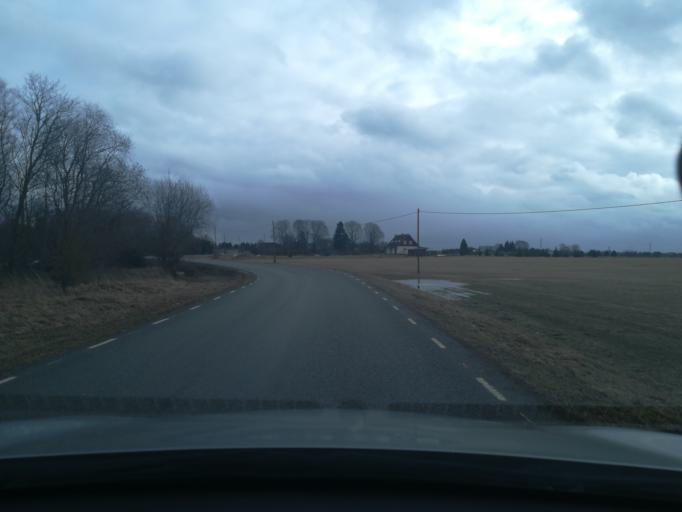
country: EE
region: Harju
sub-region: Saue linn
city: Saue
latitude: 59.3456
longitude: 24.5430
